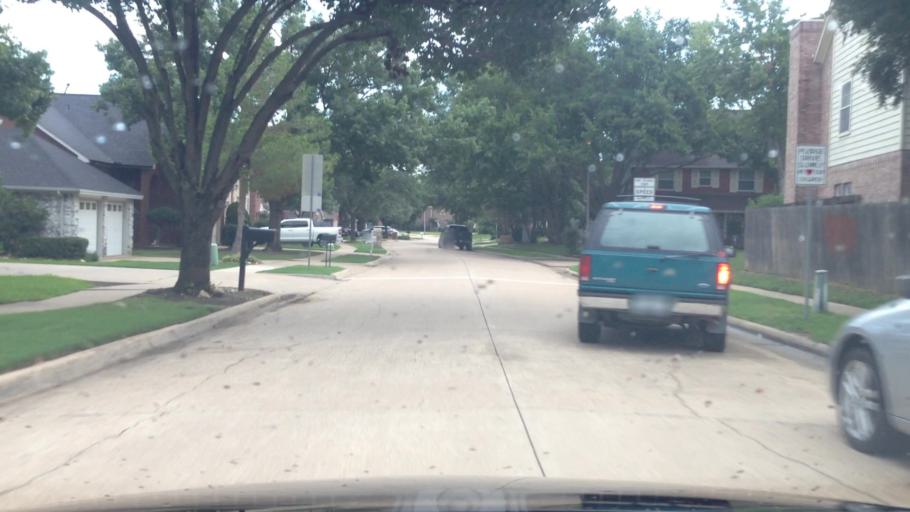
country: US
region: Texas
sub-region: Denton County
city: Flower Mound
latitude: 33.0192
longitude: -97.0636
